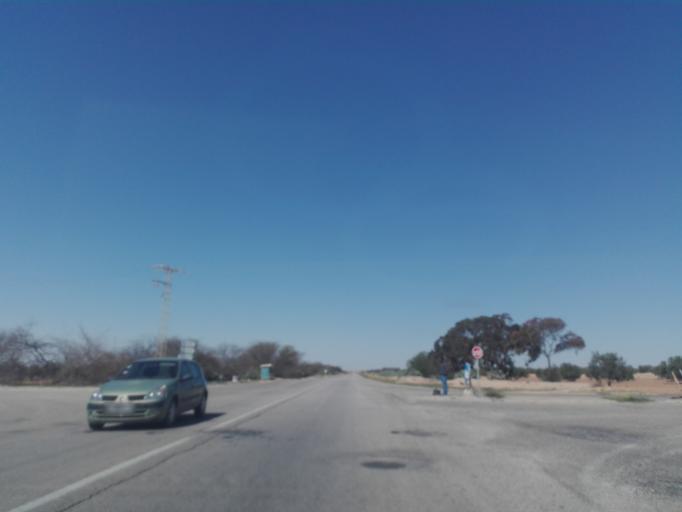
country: TN
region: Safaqis
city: Bi'r `Ali Bin Khalifah
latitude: 34.7574
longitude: 10.2708
